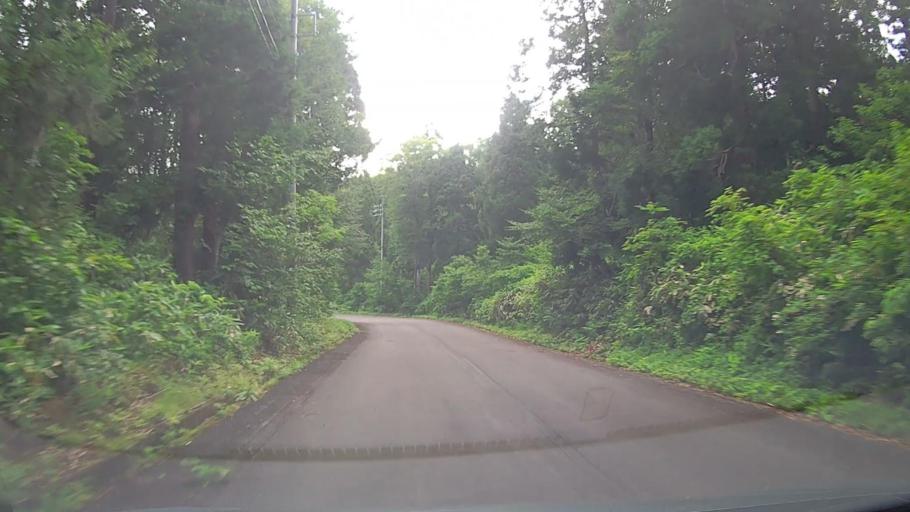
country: JP
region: Nagano
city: Iiyama
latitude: 36.9175
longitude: 138.4836
